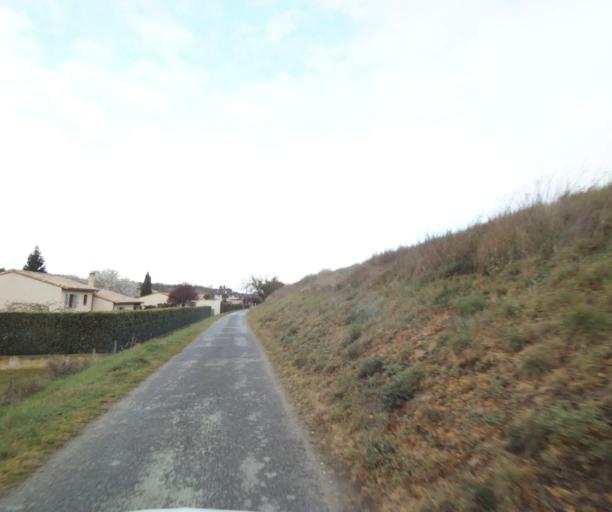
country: FR
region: Midi-Pyrenees
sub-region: Departement de l'Ariege
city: Saverdun
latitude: 43.2276
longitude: 1.5907
